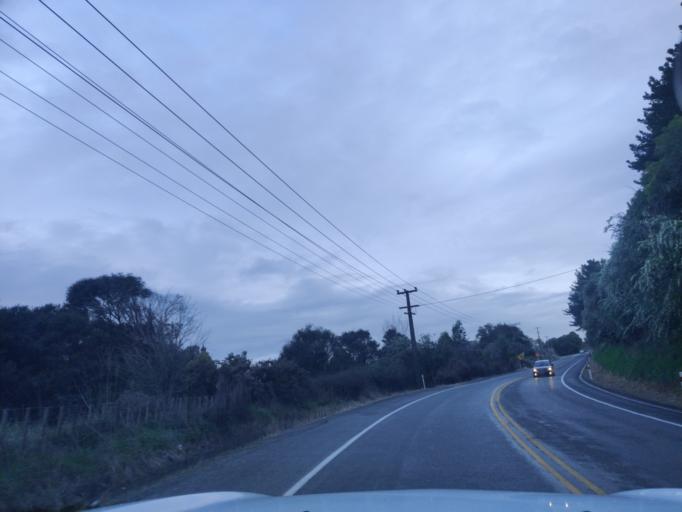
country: NZ
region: Manawatu-Wanganui
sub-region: Palmerston North City
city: Palmerston North
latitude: -40.3789
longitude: 175.6485
